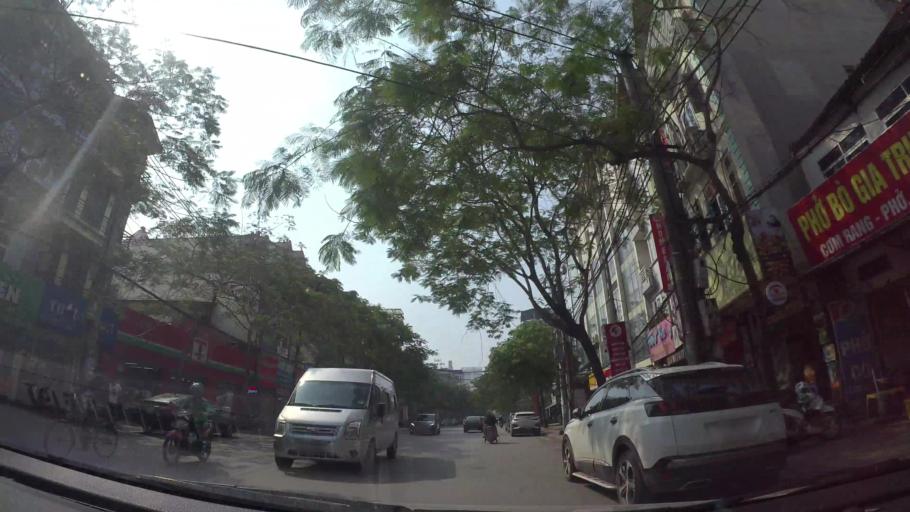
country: VN
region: Ha Noi
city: Tay Ho
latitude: 21.0617
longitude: 105.8085
